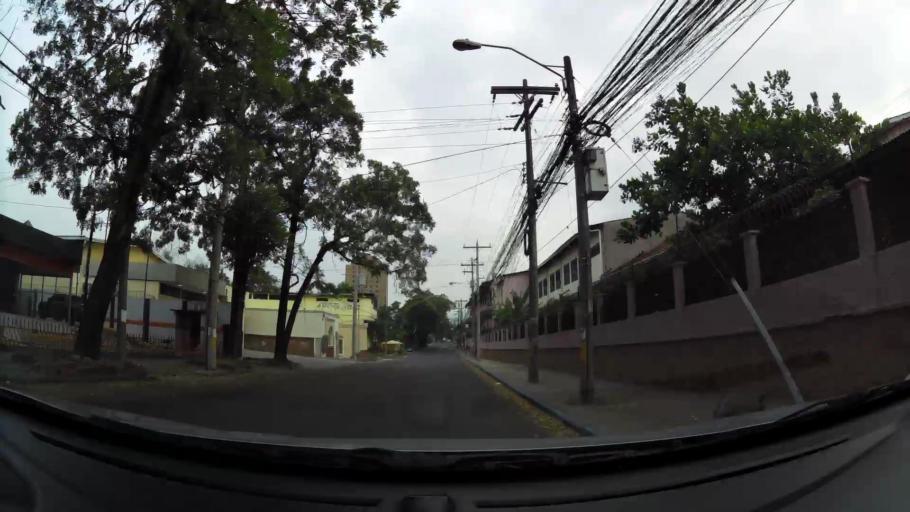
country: HN
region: Cortes
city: San Pedro Sula
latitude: 15.5096
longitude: -88.0308
